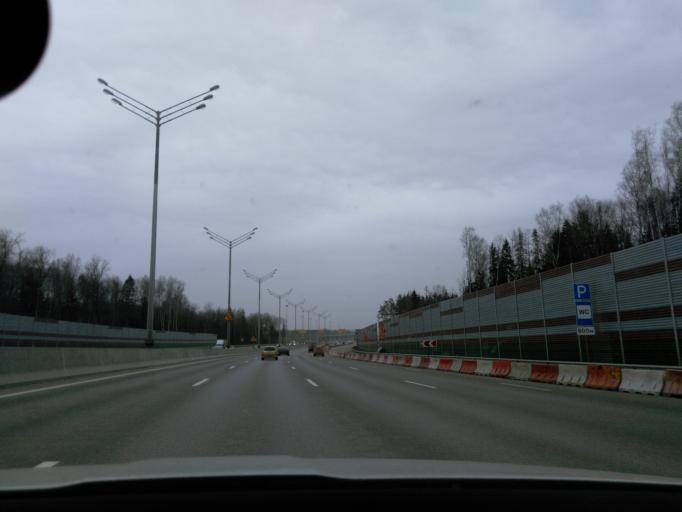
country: RU
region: Moscow
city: Khimki
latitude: 55.9421
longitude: 37.4478
